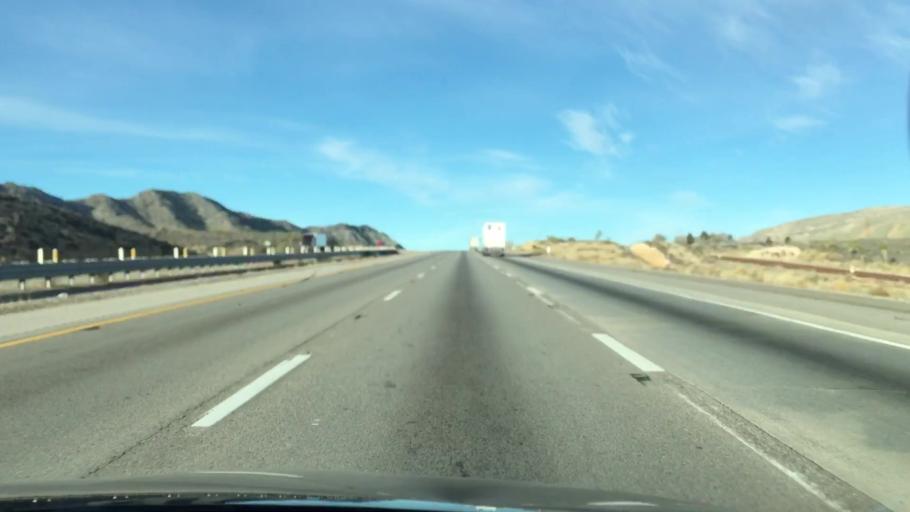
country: US
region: Nevada
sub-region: Clark County
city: Sandy Valley
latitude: 35.4691
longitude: -115.5344
